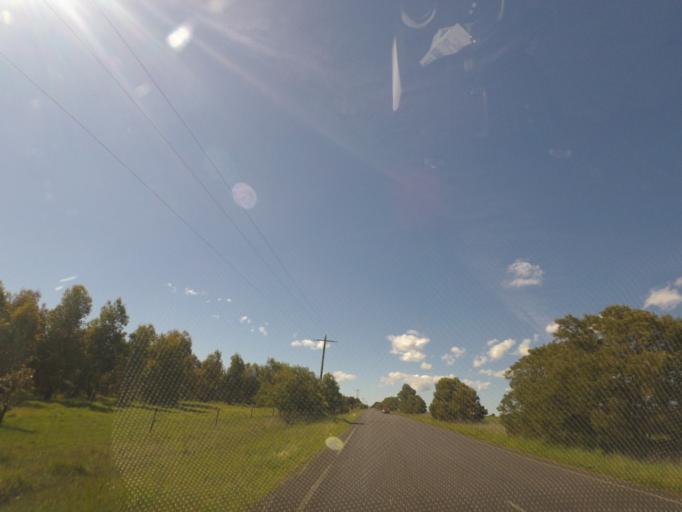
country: AU
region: Victoria
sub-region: Moorabool
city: Bacchus Marsh
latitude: -37.7068
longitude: 144.2226
